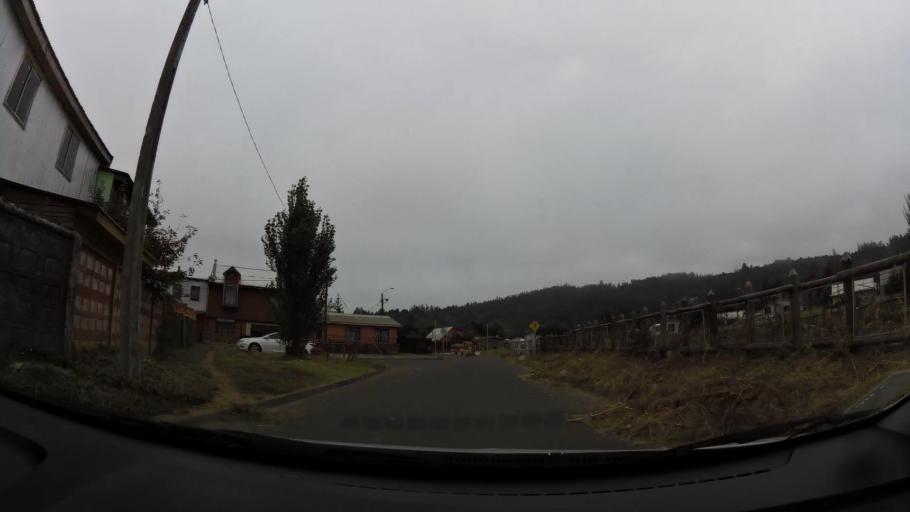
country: CL
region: Biobio
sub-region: Provincia de Concepcion
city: Concepcion
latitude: -36.8283
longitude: -73.0077
